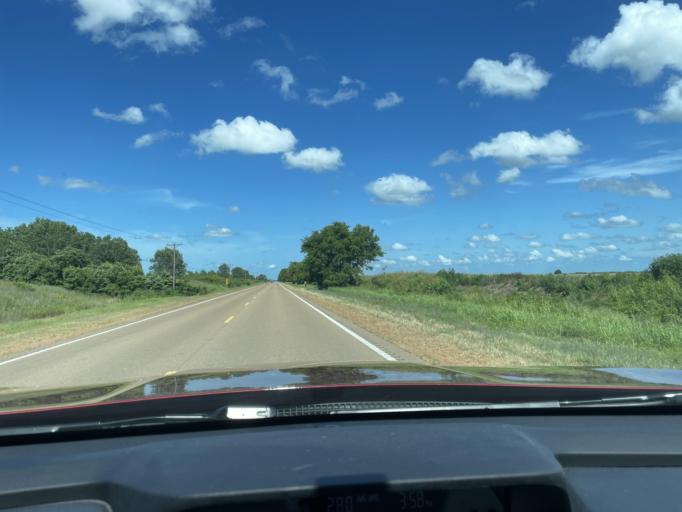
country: US
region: Mississippi
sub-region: Humphreys County
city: Belzoni
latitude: 33.1837
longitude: -90.5905
